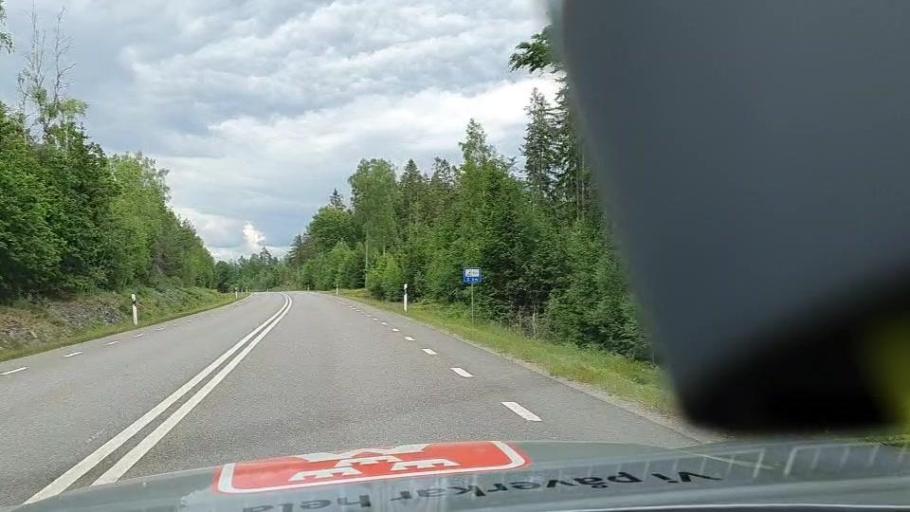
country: SE
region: Kalmar
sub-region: Emmaboda Kommun
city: Emmaboda
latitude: 56.4553
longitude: 15.5834
